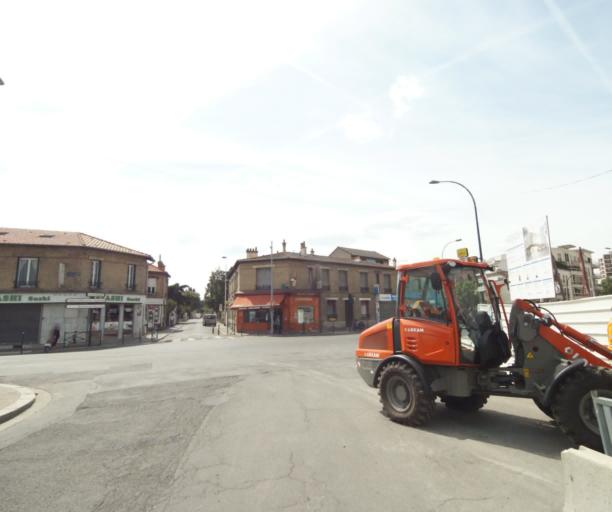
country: FR
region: Ile-de-France
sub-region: Departement des Hauts-de-Seine
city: Bois-Colombes
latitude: 48.9318
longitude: 2.2670
